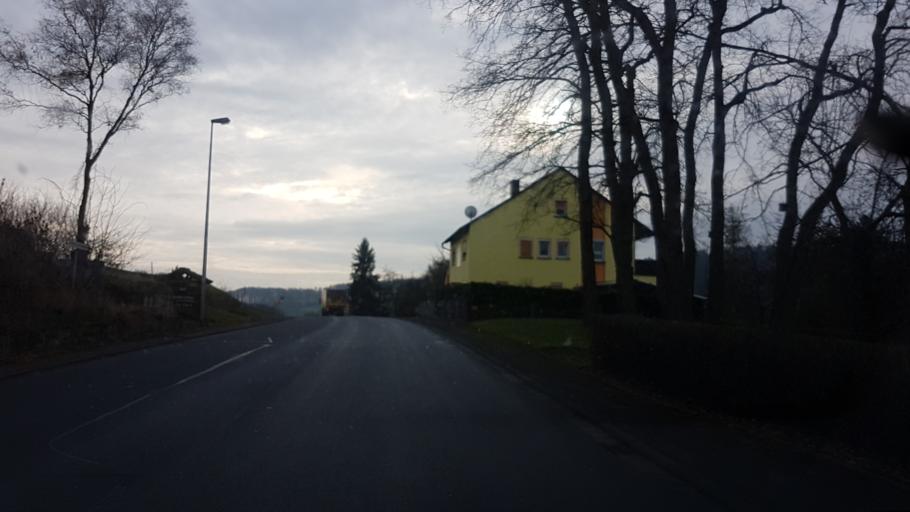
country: DE
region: Bavaria
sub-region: Regierungsbezirk Unterfranken
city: Pfarrweisach
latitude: 50.1683
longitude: 10.7196
